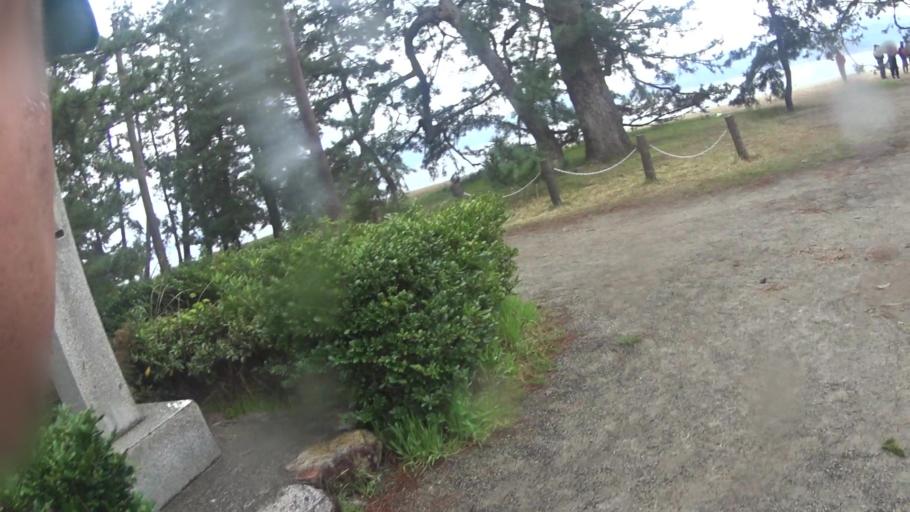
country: JP
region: Kyoto
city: Miyazu
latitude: 35.5770
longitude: 135.1979
